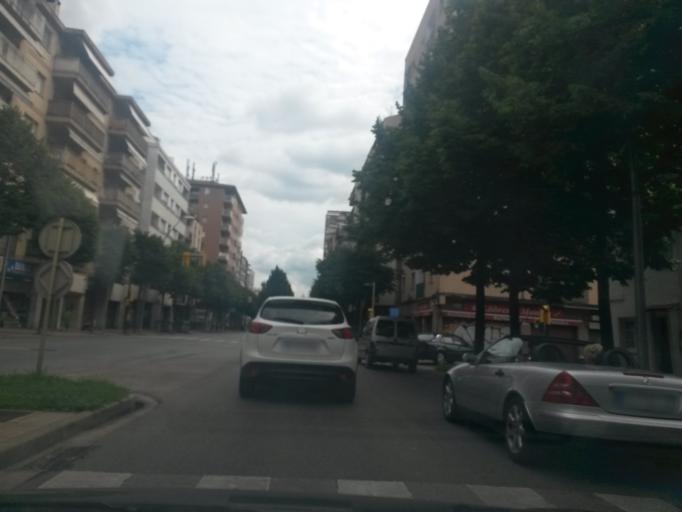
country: ES
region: Catalonia
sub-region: Provincia de Girona
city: Salt
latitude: 41.9723
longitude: 2.7898
